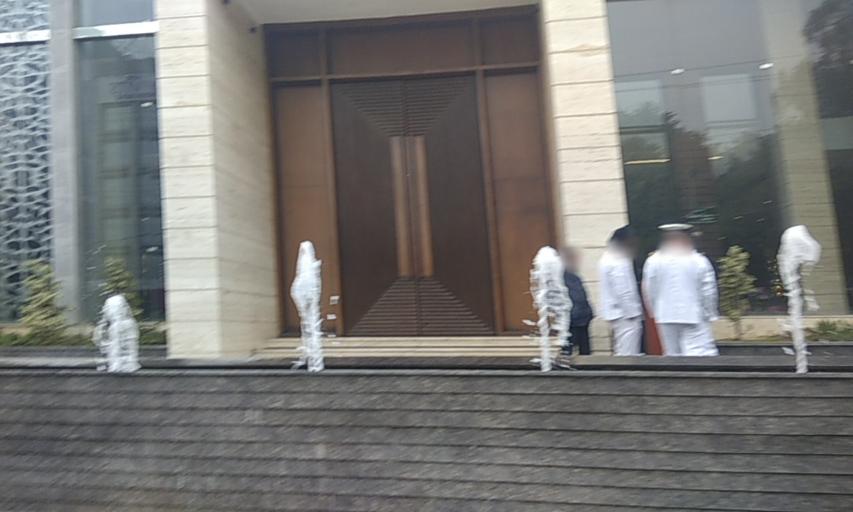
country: IN
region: Punjab
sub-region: Amritsar
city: Amritsar
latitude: 31.6409
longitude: 74.8668
